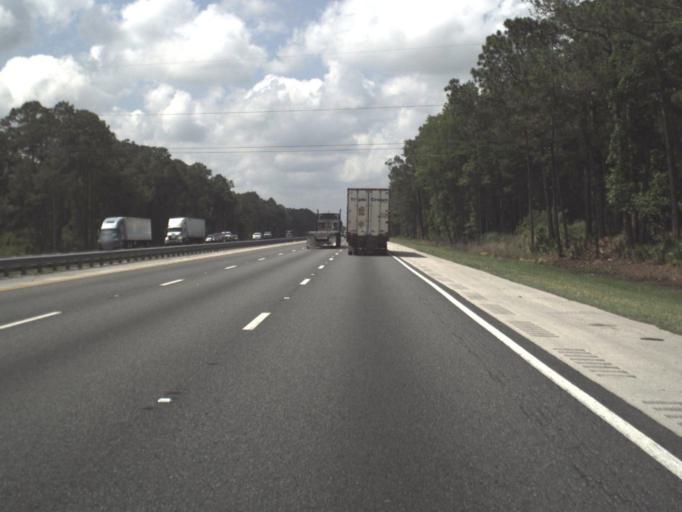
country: US
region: Florida
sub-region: Saint Johns County
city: Saint Augustine
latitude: 29.8731
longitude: -81.3984
